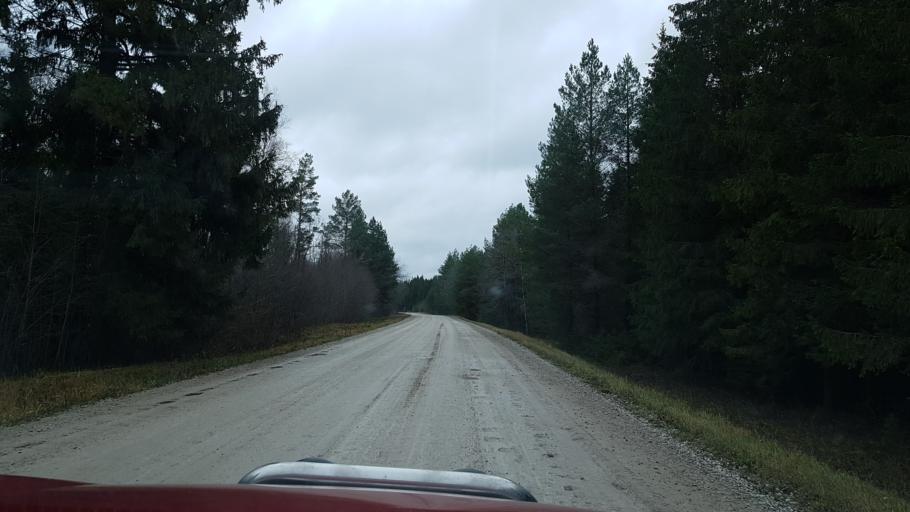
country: EE
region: Paernumaa
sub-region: Halinga vald
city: Parnu-Jaagupi
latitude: 58.5546
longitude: 24.4124
